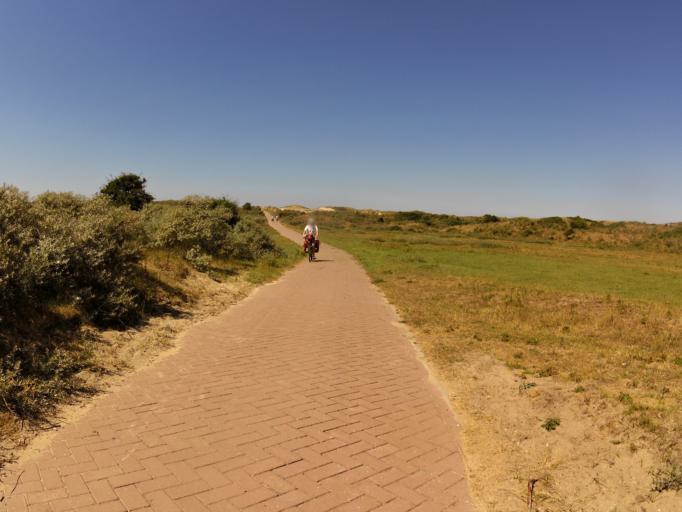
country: NL
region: North Holland
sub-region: Gemeente Zandvoort
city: Zandvoort
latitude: 52.4250
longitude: 4.5666
